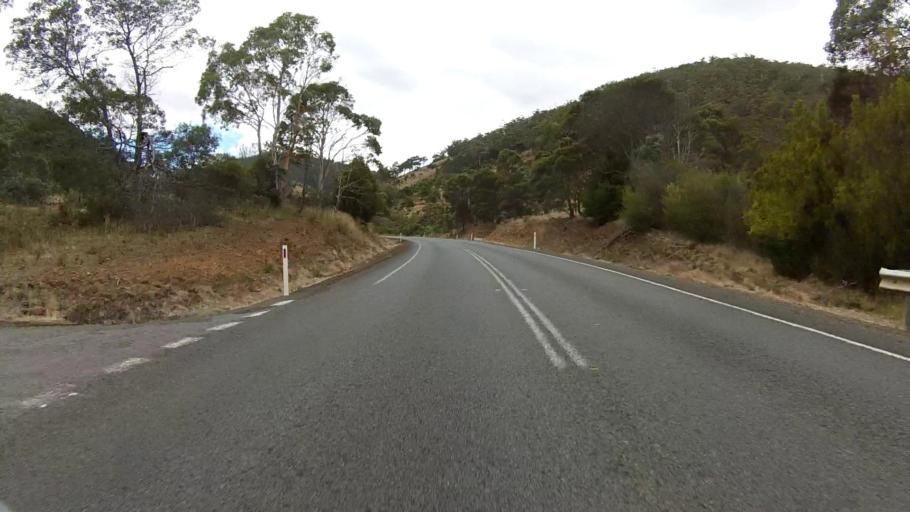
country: AU
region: Tasmania
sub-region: Sorell
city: Sorell
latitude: -42.6818
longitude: 147.5304
